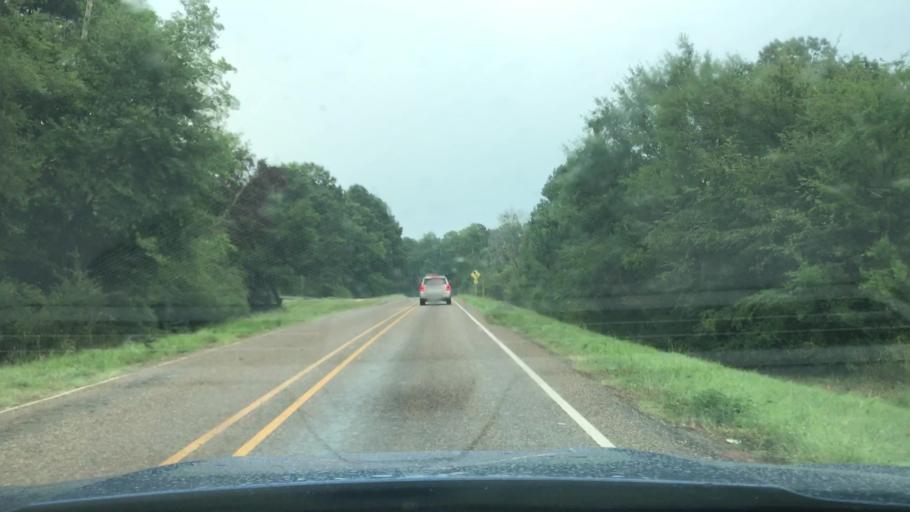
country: US
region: Texas
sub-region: Harrison County
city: Waskom
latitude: 32.4829
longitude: -94.1129
